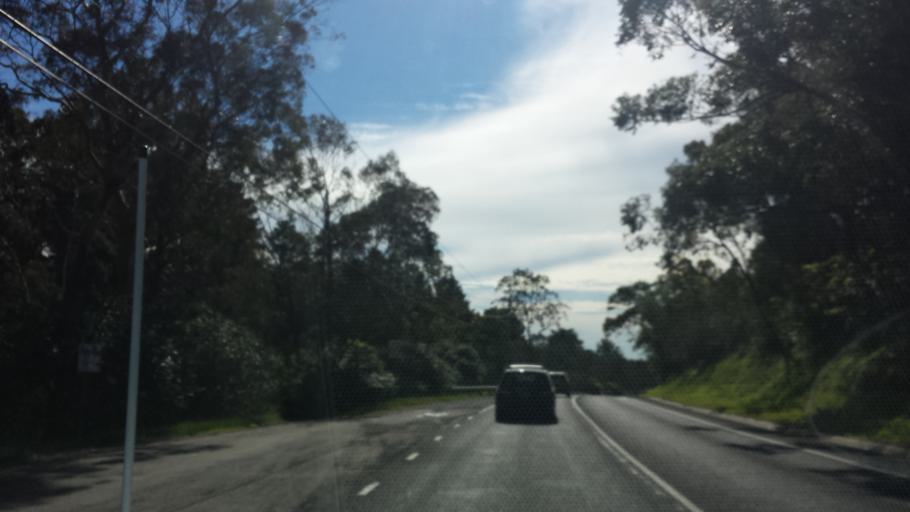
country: AU
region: Victoria
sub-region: Maroondah
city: Warranwood
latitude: -37.7804
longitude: 145.2336
